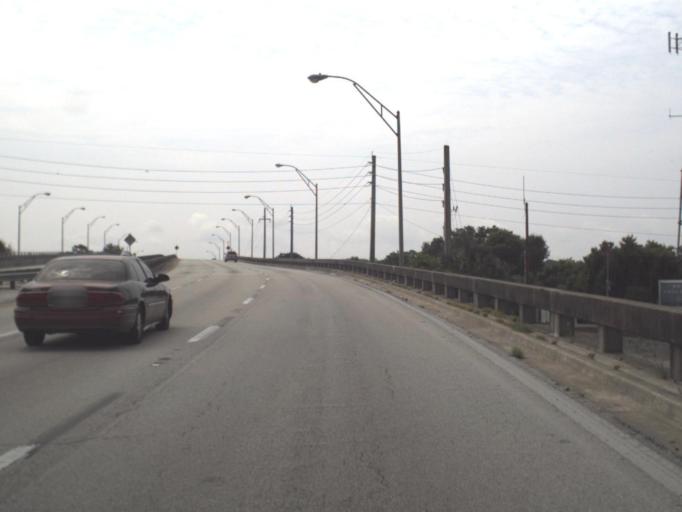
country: US
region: Florida
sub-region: Duval County
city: Jacksonville
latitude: 30.2761
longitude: -81.7193
